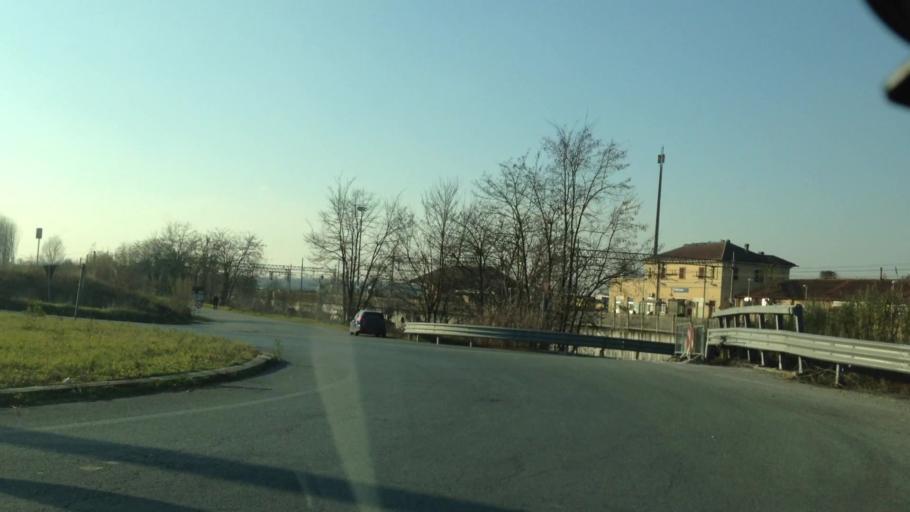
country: IT
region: Piedmont
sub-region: Provincia di Alessandria
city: Felizzano
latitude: 44.8931
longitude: 8.4388
